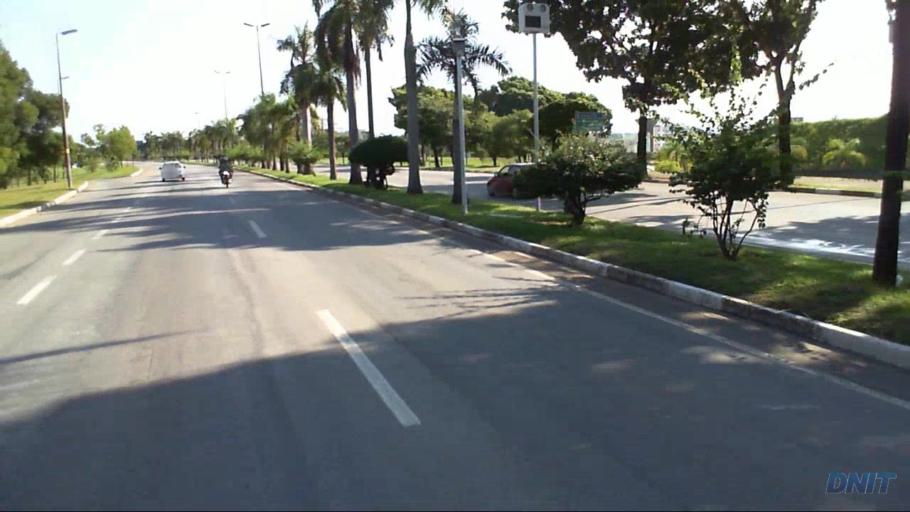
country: BR
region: Minas Gerais
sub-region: Ipatinga
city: Ipatinga
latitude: -19.4715
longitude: -42.5397
